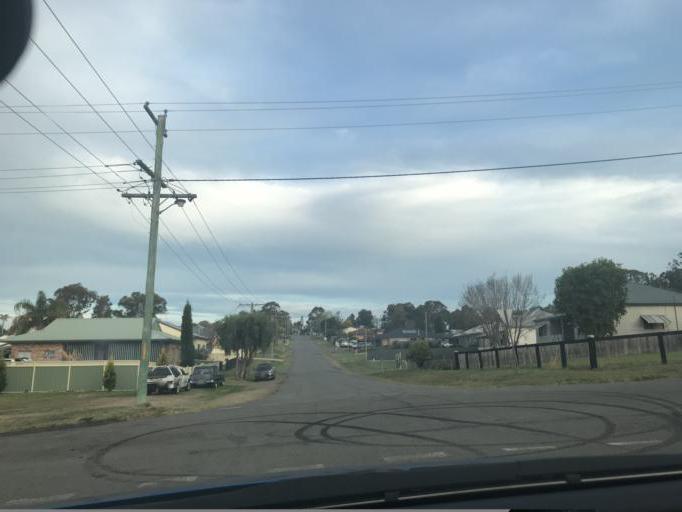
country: AU
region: New South Wales
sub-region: Cessnock
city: Cessnock
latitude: -32.9030
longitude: 151.2825
